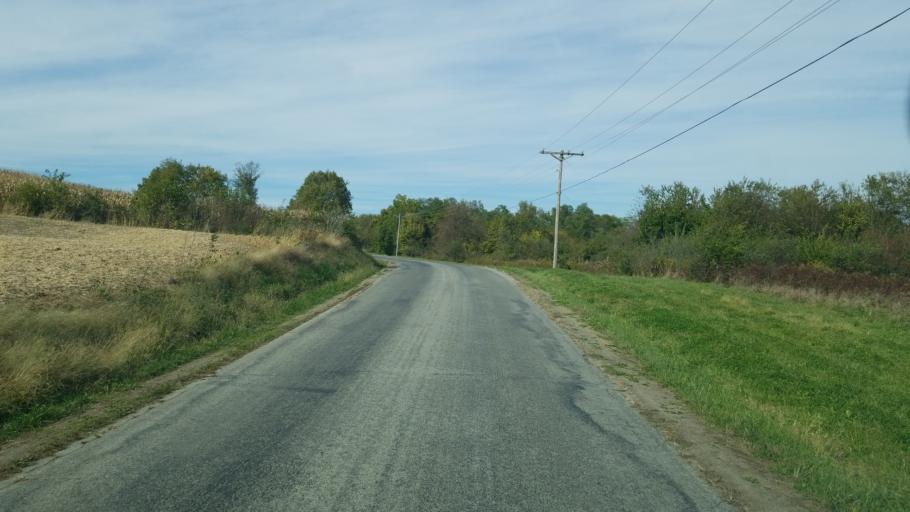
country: US
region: Ohio
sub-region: Highland County
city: Greenfield
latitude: 39.3100
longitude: -83.4629
